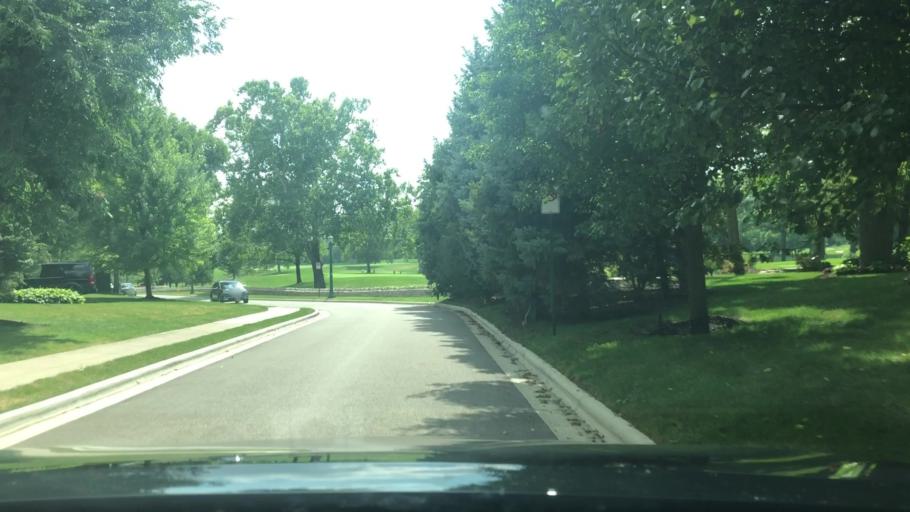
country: US
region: Ohio
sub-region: Franklin County
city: Upper Arlington
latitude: 40.0019
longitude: -83.0690
